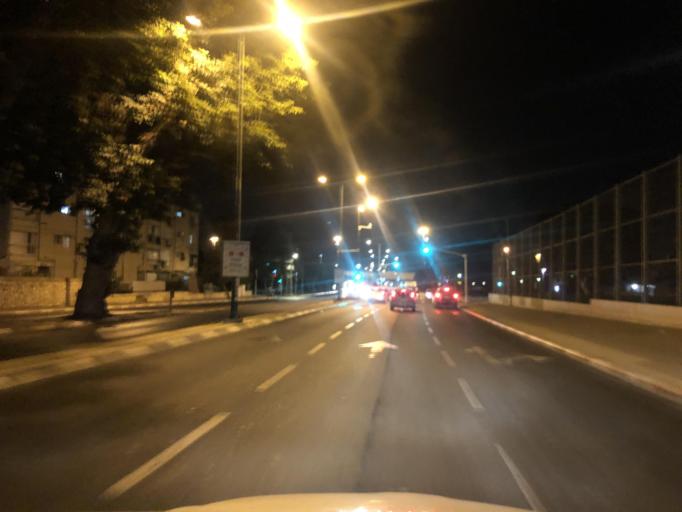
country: IL
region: Tel Aviv
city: Yafo
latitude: 32.0474
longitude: 34.7798
